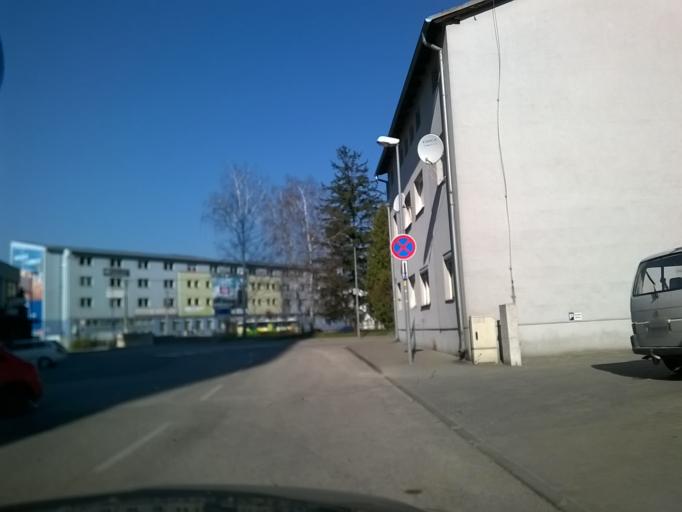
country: SK
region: Zilinsky
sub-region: Okres Zilina
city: Zilina
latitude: 49.2299
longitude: 18.7417
